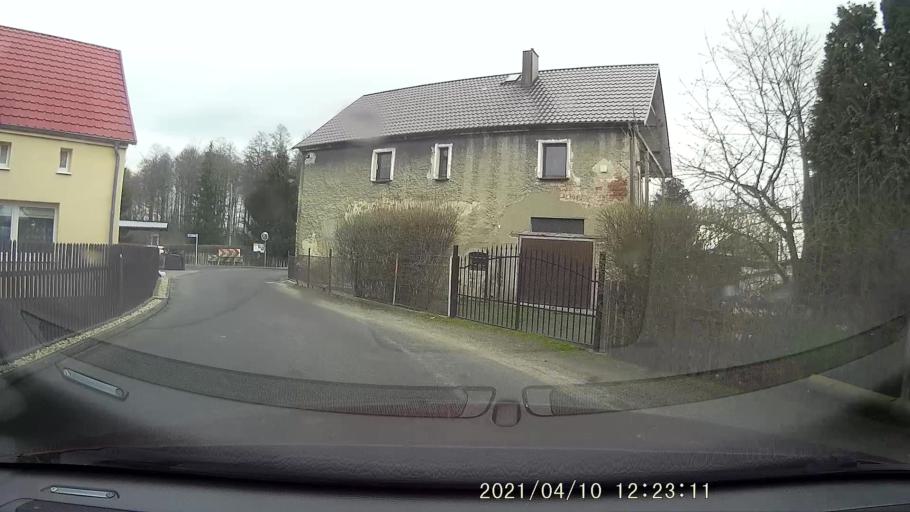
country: PL
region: Lower Silesian Voivodeship
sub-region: Powiat zgorzelecki
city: Lagow
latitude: 51.1642
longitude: 15.0394
